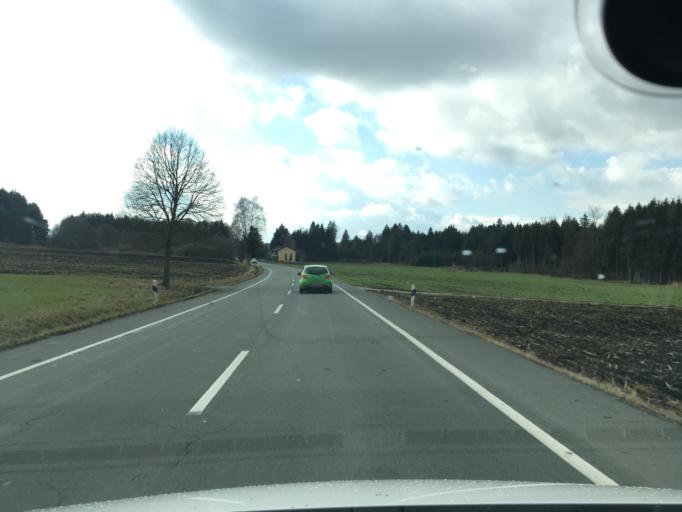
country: DE
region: Bavaria
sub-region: Upper Bavaria
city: Riedering
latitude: 47.8368
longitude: 12.1921
